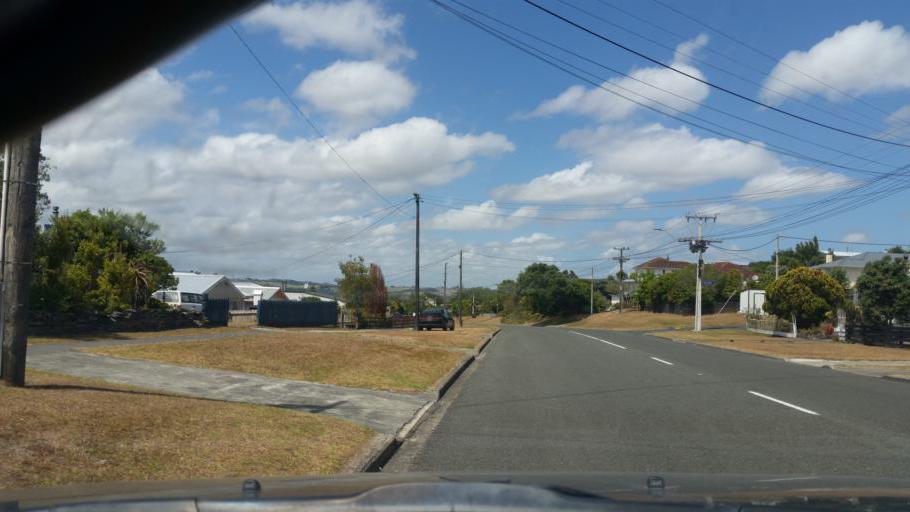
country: NZ
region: Northland
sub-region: Kaipara District
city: Dargaville
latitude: -35.9299
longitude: 173.8534
